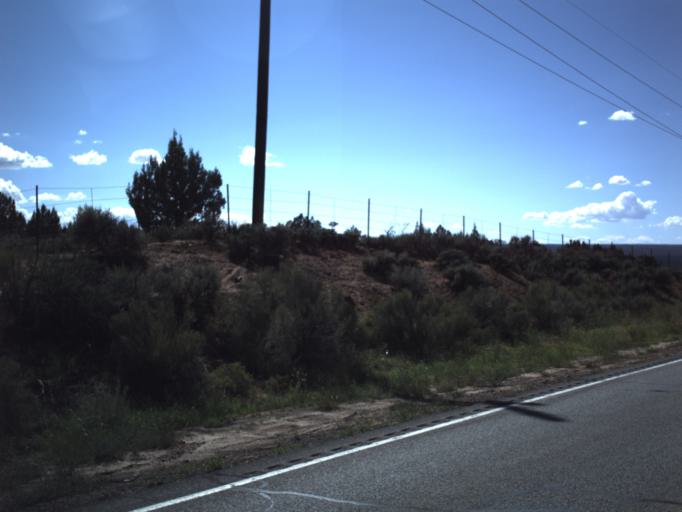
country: US
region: Arizona
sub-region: Mohave County
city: Colorado City
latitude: 37.0206
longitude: -113.0360
